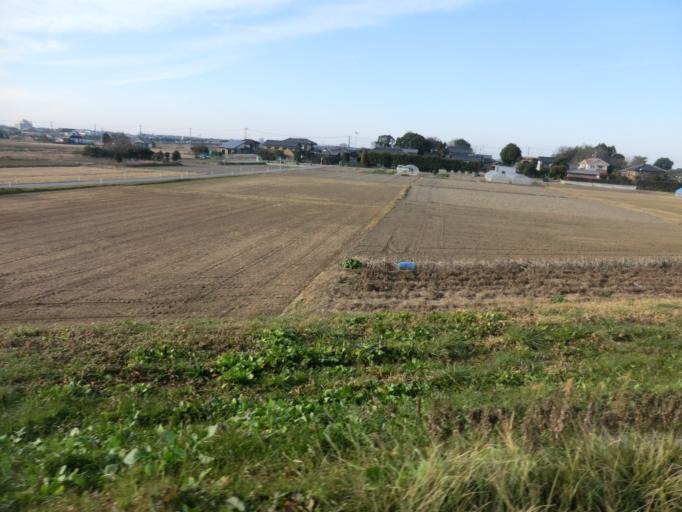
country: JP
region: Ibaraki
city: Mitsukaido
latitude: 36.0238
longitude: 140.0091
